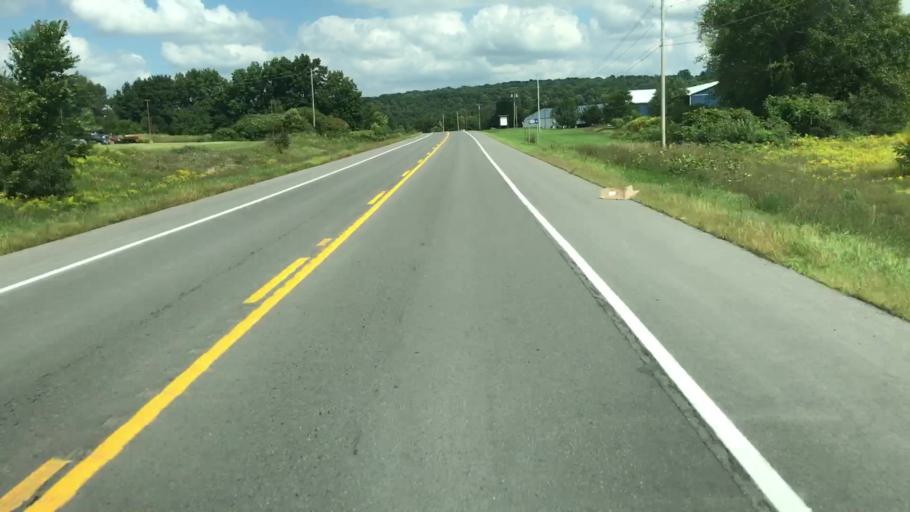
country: US
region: New York
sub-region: Onondaga County
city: Marcellus
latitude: 42.9530
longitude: -76.3481
